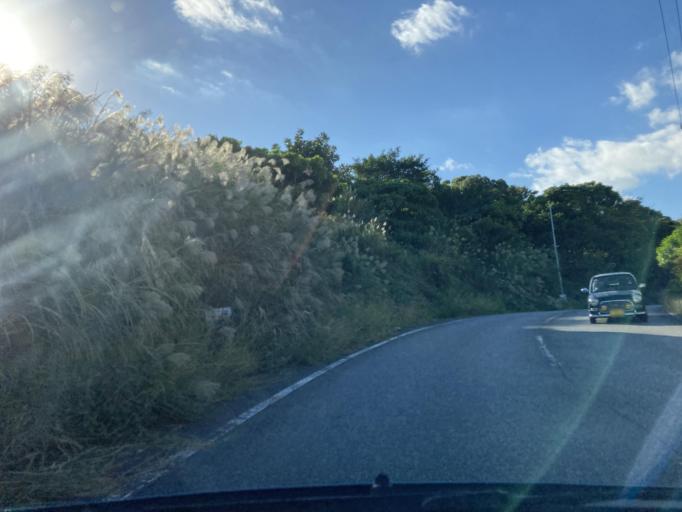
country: JP
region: Okinawa
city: Ginowan
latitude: 26.2206
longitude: 127.7572
